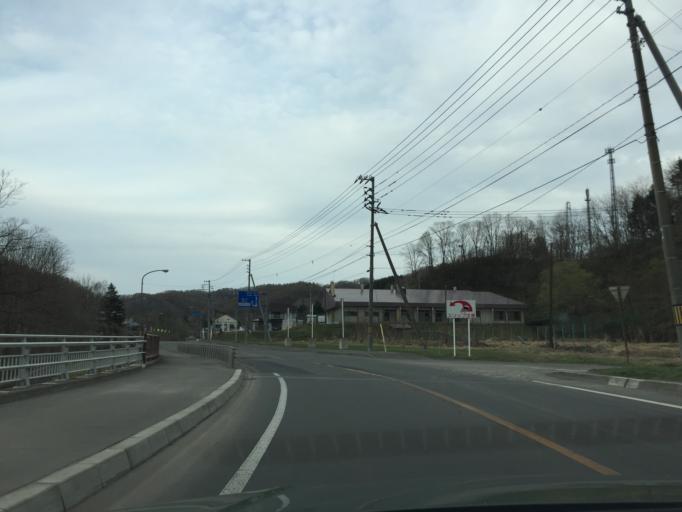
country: JP
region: Hokkaido
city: Utashinai
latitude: 43.5059
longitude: 142.0199
